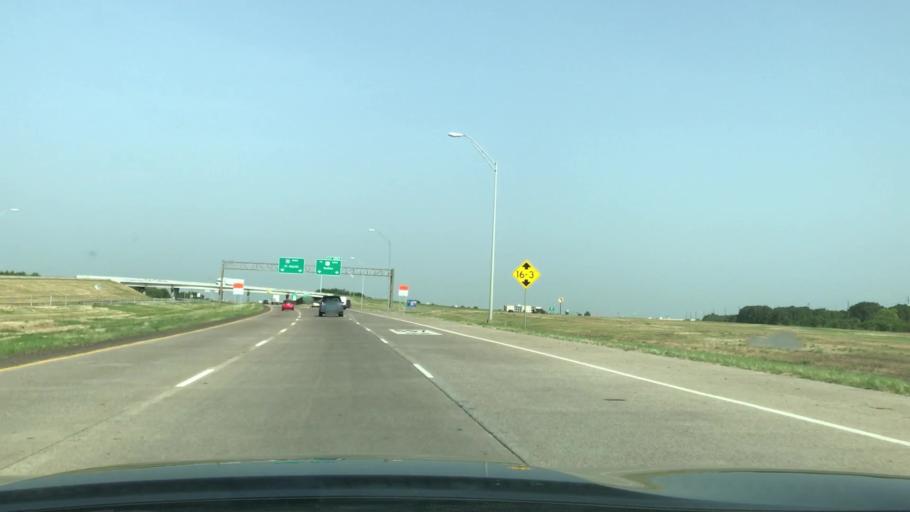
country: US
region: Texas
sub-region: Kaufman County
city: Terrell
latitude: 32.7142
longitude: -96.3055
